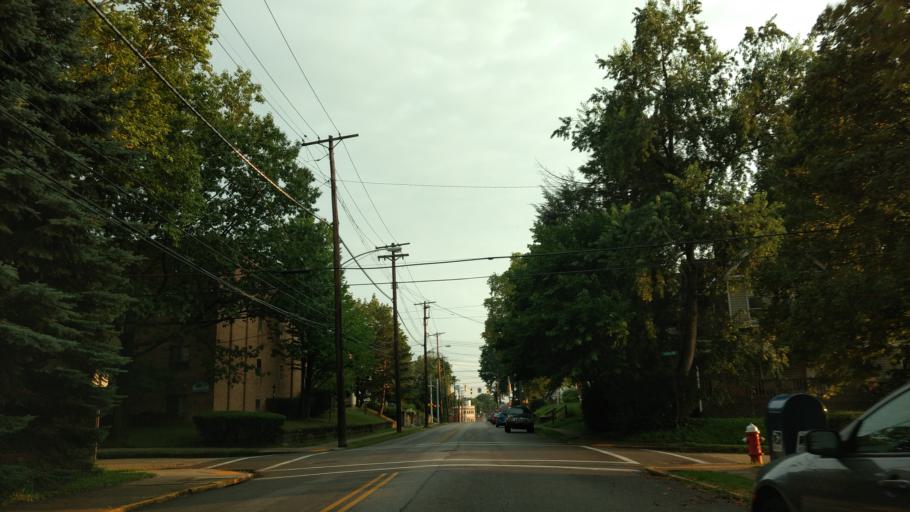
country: US
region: Pennsylvania
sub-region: Allegheny County
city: Bellevue
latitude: 40.4984
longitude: -80.0536
